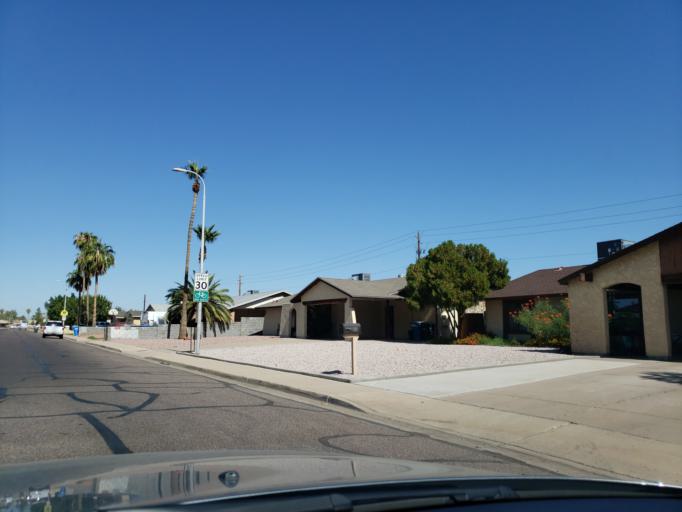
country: US
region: Arizona
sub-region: Maricopa County
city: Tolleson
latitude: 33.4978
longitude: -112.2296
